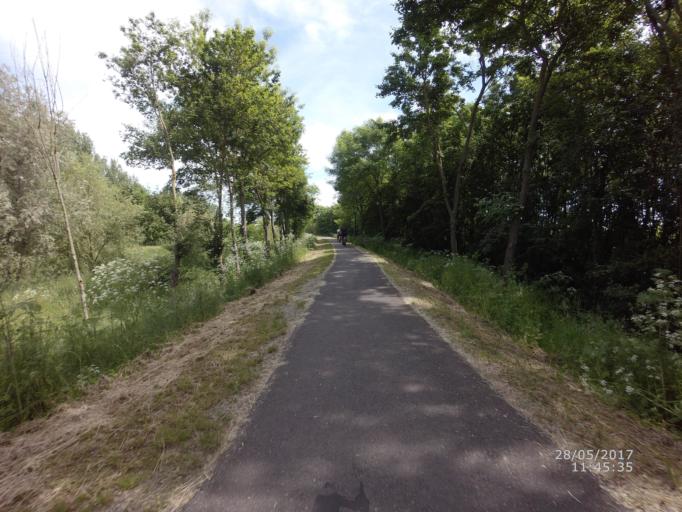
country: DE
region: Thuringia
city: Griefstedt
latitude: 51.1954
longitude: 11.1316
